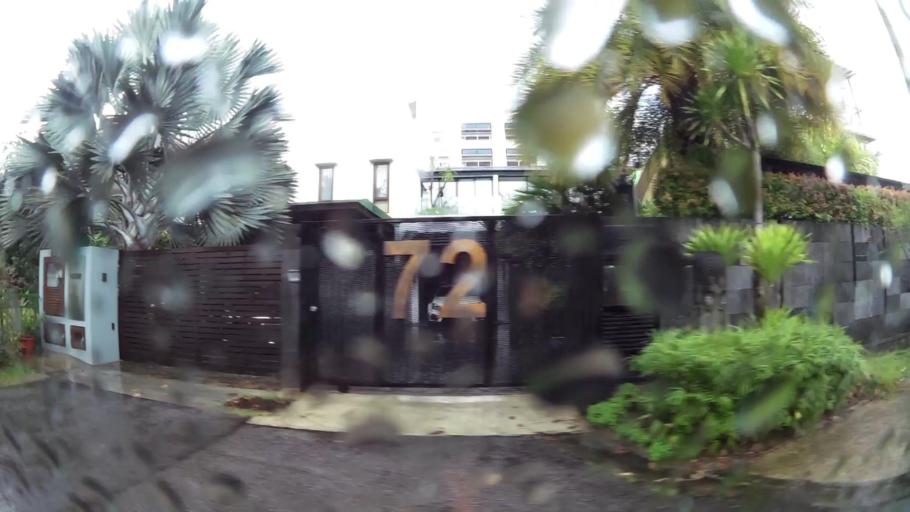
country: SG
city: Singapore
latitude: 1.3342
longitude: 103.9472
